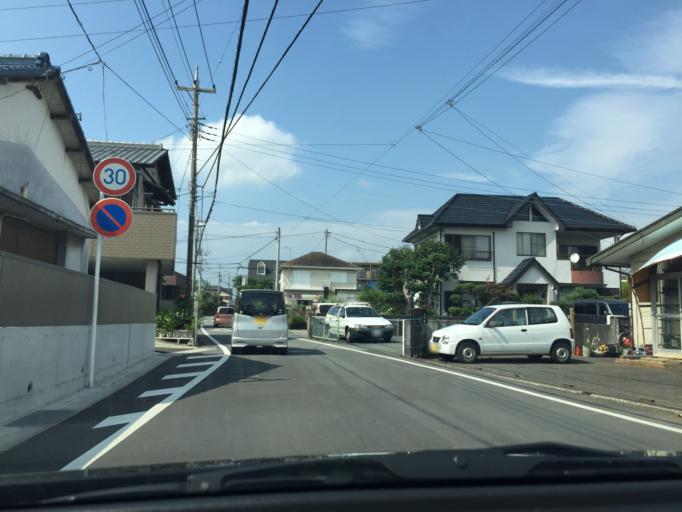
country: JP
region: Shizuoka
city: Mishima
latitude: 35.1395
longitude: 138.9000
